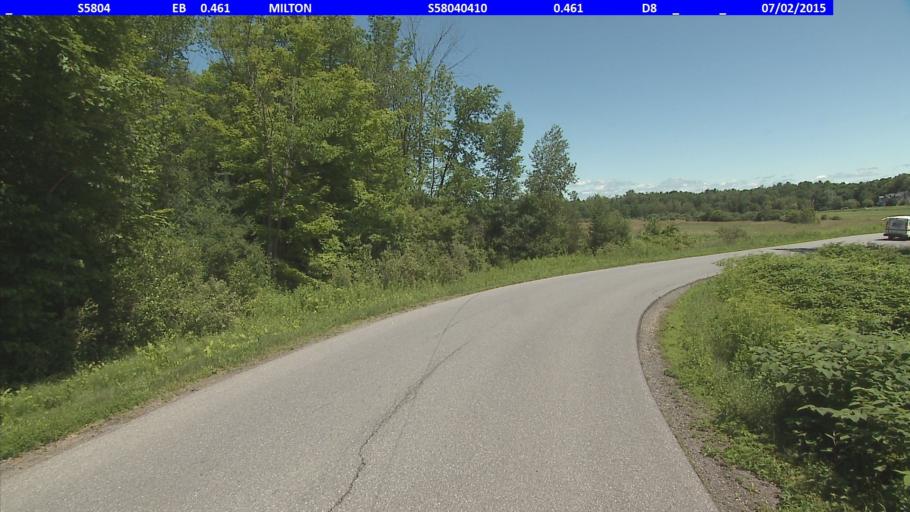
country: US
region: Vermont
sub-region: Chittenden County
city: Milton
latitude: 44.6535
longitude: -73.1630
